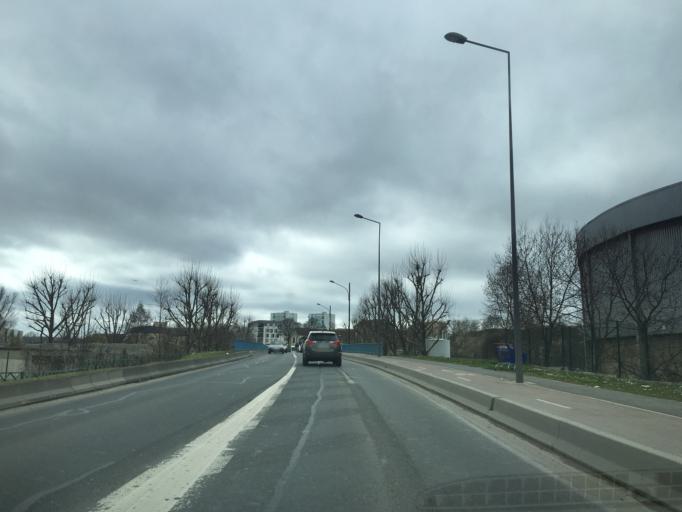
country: FR
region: Ile-de-France
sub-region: Departement du Val-de-Marne
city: Bonneuil-sur-Marne
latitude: 48.7779
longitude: 2.4910
